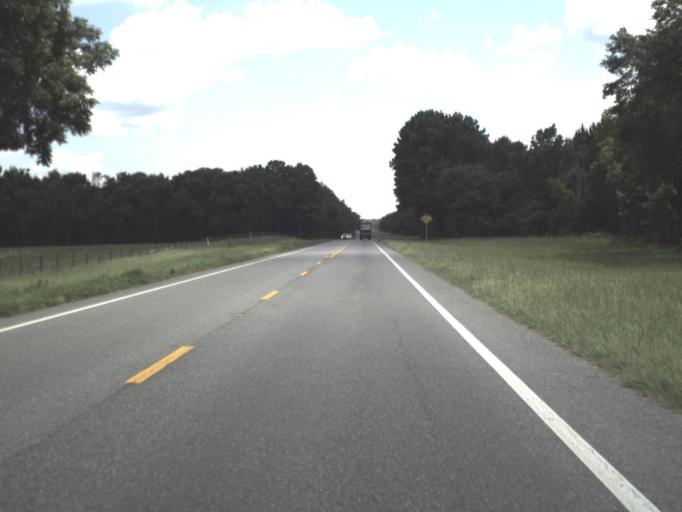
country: US
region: Florida
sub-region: Columbia County
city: Watertown
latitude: 30.0169
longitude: -82.5975
